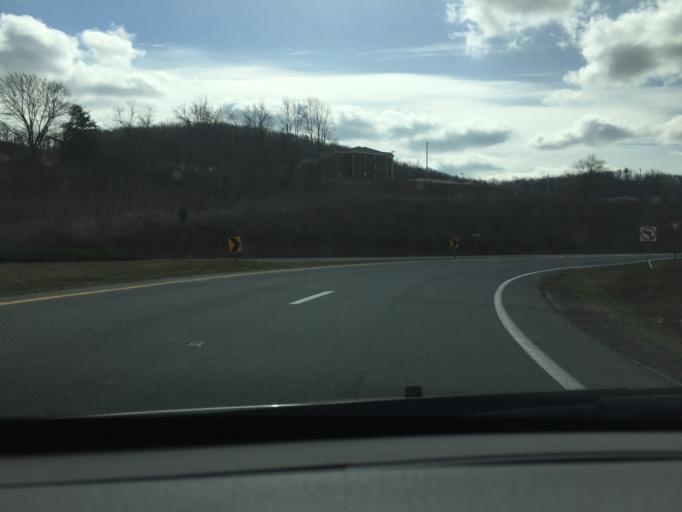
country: US
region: Virginia
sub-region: City of Lynchburg
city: West Lynchburg
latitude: 37.3548
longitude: -79.1726
